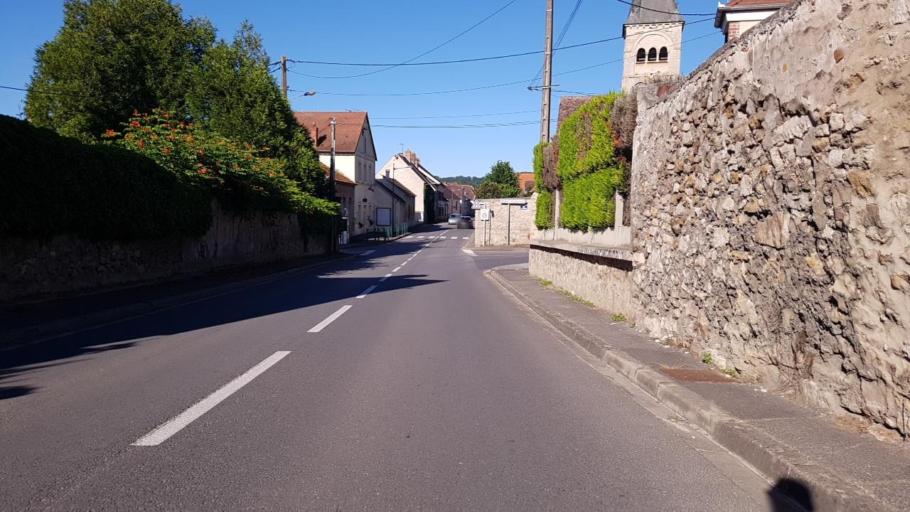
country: FR
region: Picardie
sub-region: Departement de l'Aisne
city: Chezy-sur-Marne
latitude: 49.0015
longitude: 3.3672
